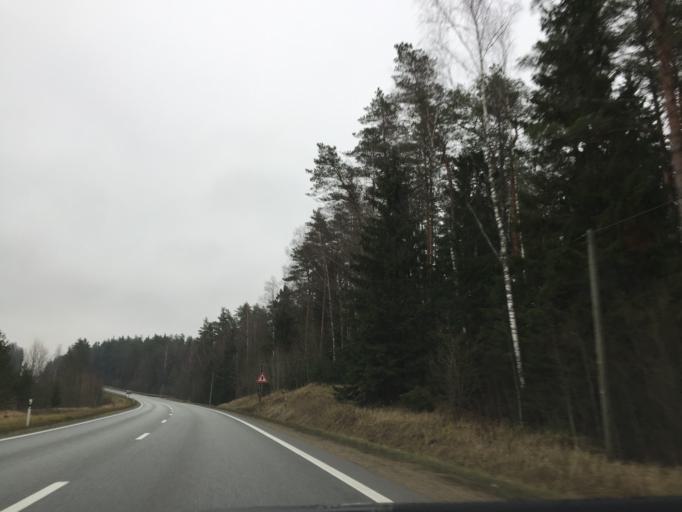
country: LV
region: Sigulda
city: Sigulda
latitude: 57.2797
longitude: 24.9073
